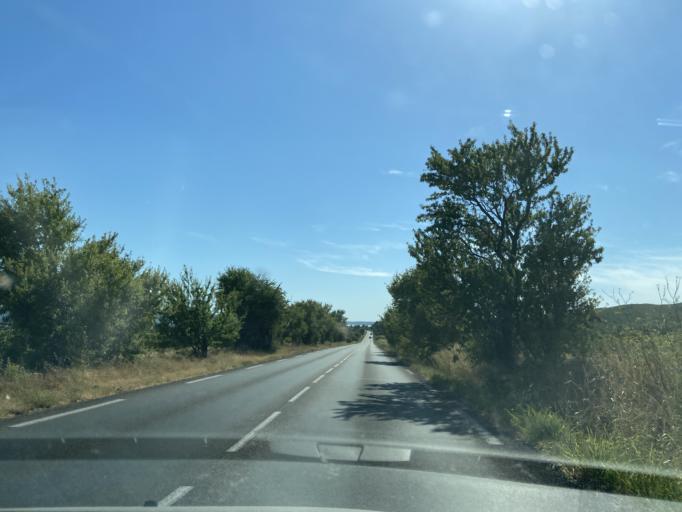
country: FR
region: Provence-Alpes-Cote d'Azur
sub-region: Departement des Bouches-du-Rhone
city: Lancon-Provence
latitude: 43.5374
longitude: 5.1195
